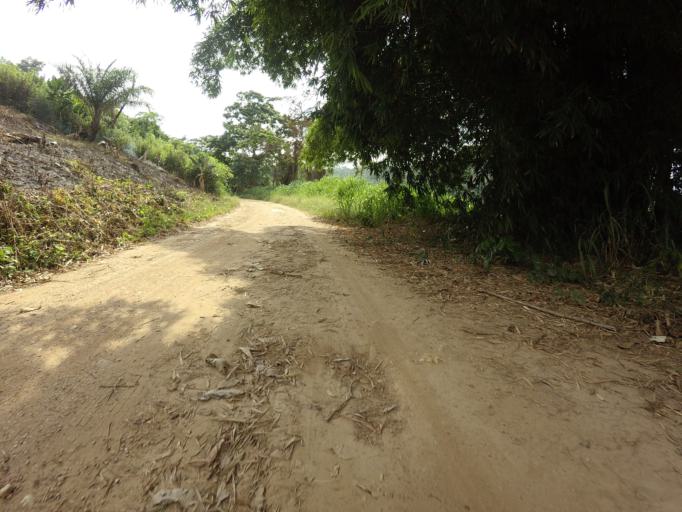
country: GH
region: Volta
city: Kpandu
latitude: 6.8753
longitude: 0.4376
